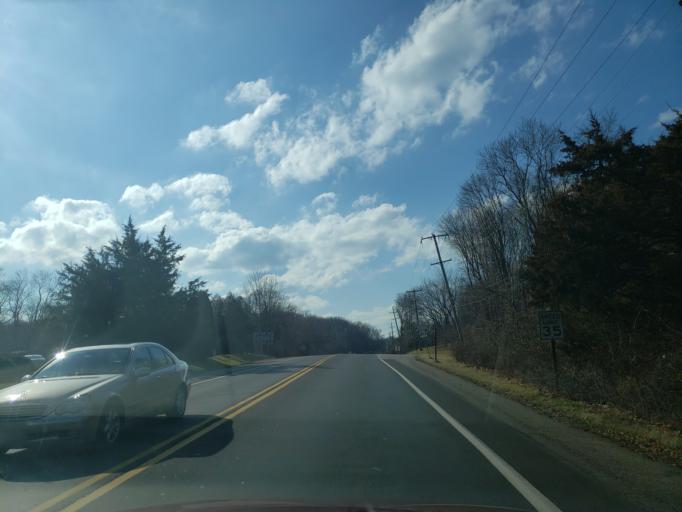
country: US
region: Pennsylvania
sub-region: Bucks County
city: Doylestown
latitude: 40.3260
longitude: -75.0587
